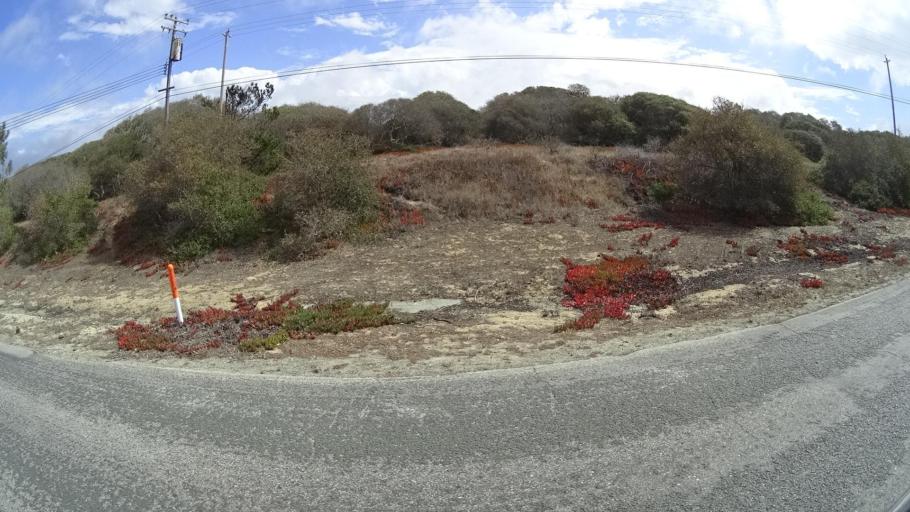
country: US
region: California
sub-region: Monterey County
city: Marina
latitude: 36.6491
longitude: -121.7911
